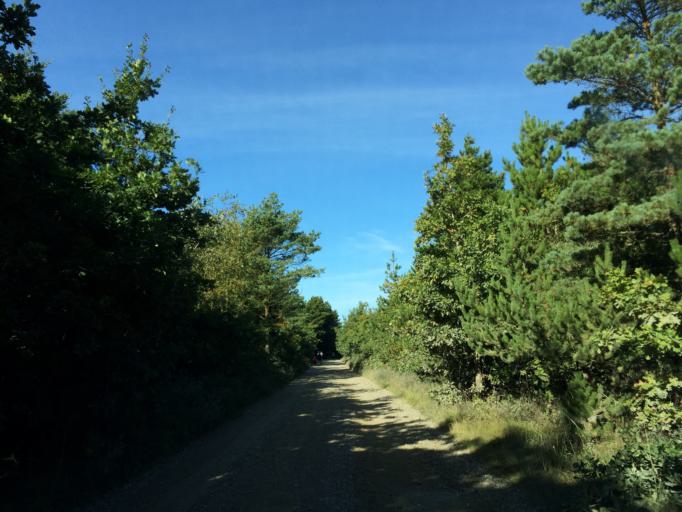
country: DK
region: Central Jutland
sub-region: Holstebro Kommune
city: Ulfborg
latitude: 56.2842
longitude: 8.1500
